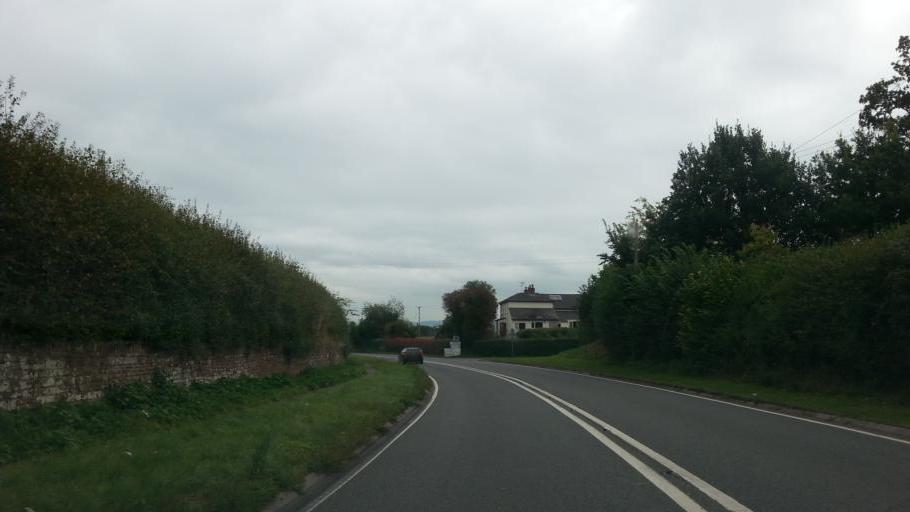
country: GB
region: England
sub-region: Gloucestershire
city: Newent
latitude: 51.8662
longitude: -2.3743
